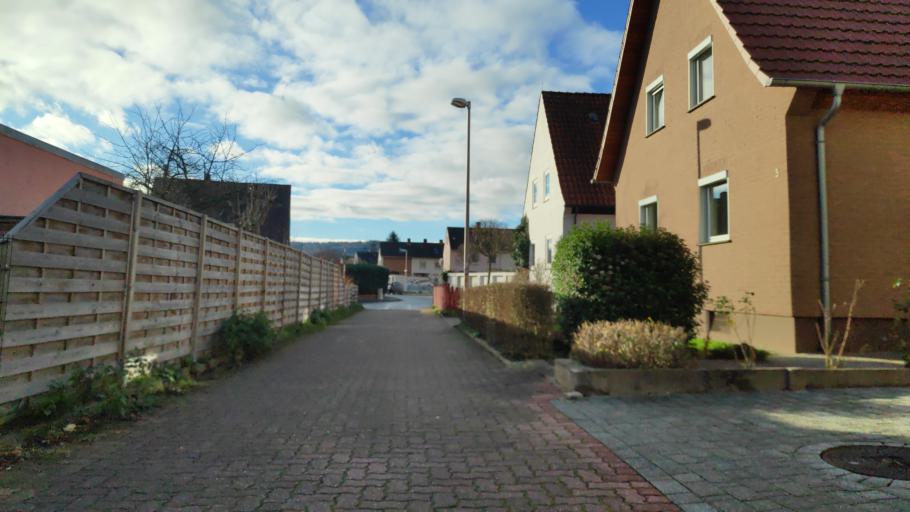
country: DE
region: North Rhine-Westphalia
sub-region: Regierungsbezirk Detmold
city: Minden
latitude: 52.2776
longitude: 8.8813
